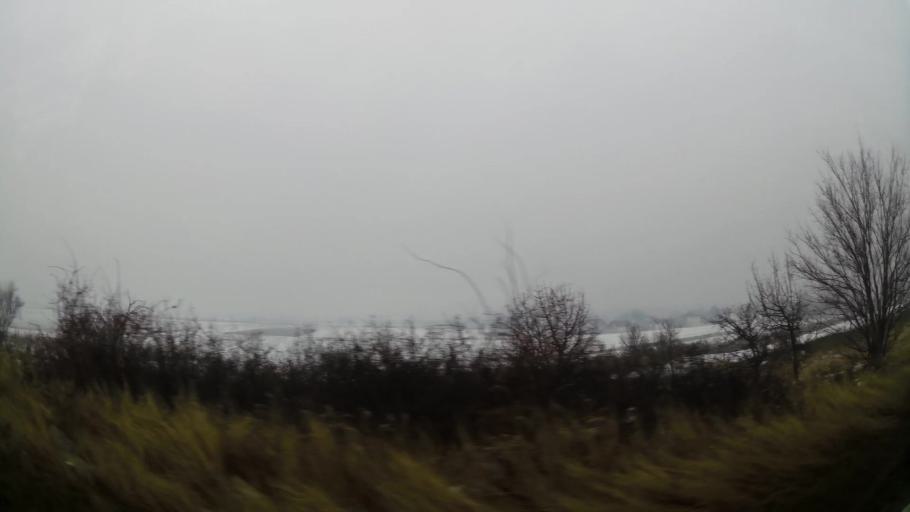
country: MK
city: Miladinovci
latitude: 41.9717
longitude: 21.6471
